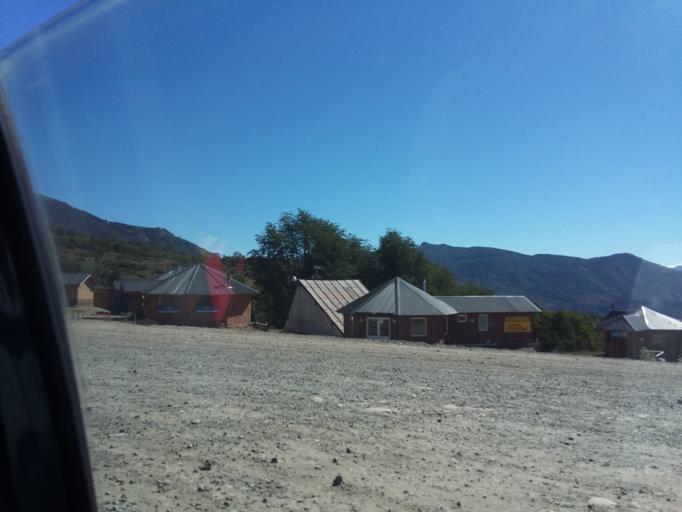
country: AR
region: Neuquen
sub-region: Departamento de Lacar
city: San Martin de los Andes
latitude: -40.1978
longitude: -71.3199
